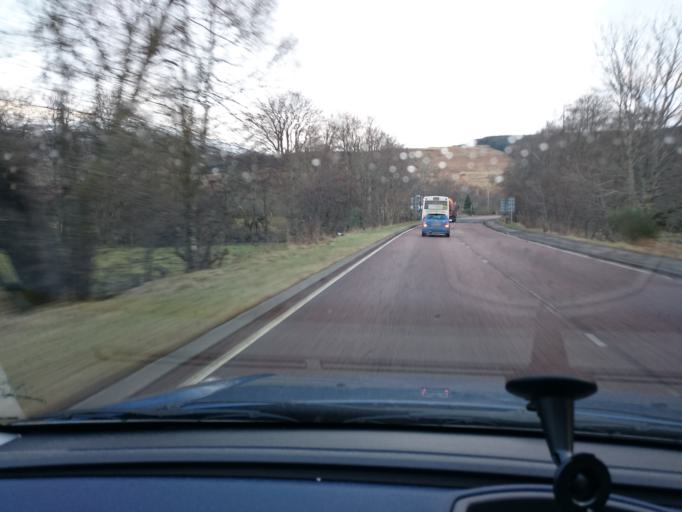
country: GB
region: Scotland
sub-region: Stirling
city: Callander
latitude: 56.3793
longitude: -4.2857
